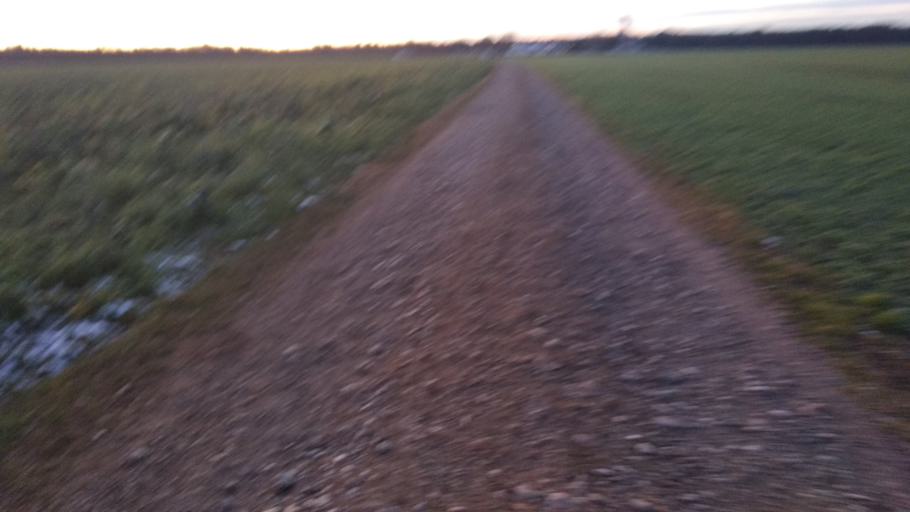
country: DE
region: Bavaria
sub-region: Upper Bavaria
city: Vaterstetten
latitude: 48.0761
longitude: 11.7829
